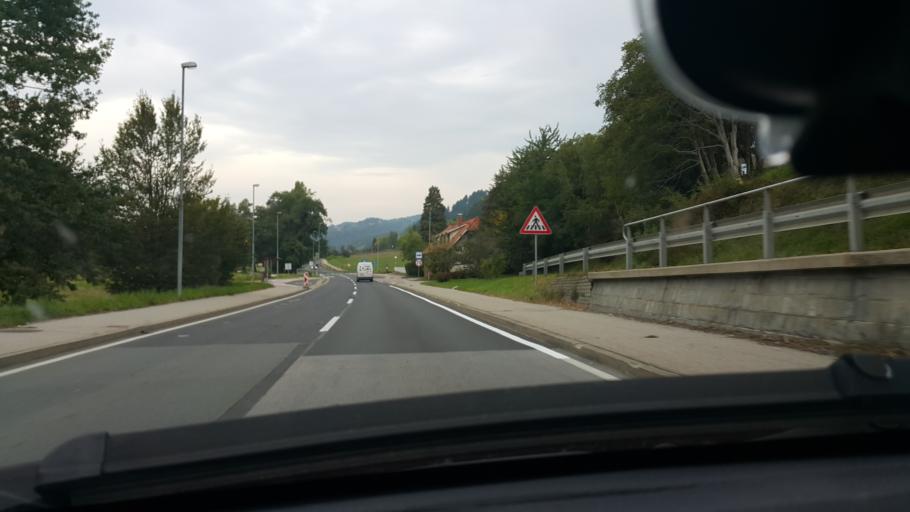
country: SI
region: Maribor
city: Kamnica
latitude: 46.5702
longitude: 15.6026
